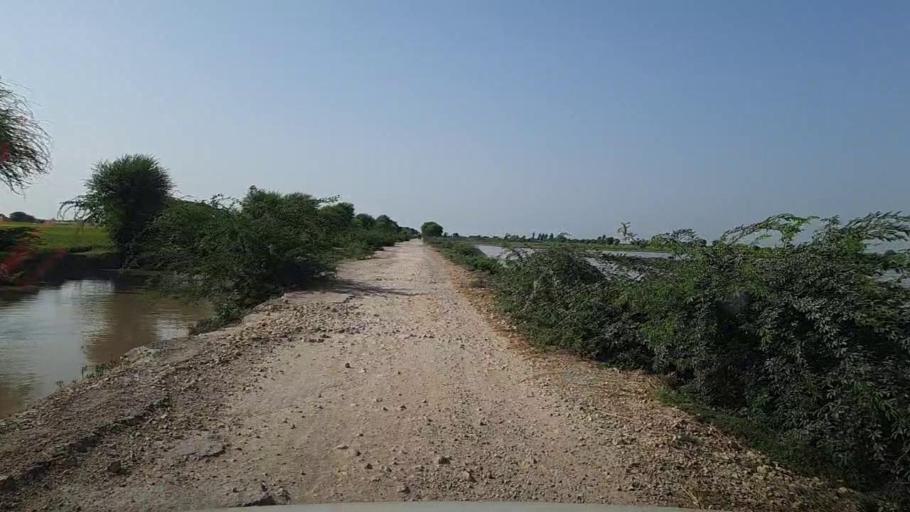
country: PK
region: Sindh
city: Kario
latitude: 24.7967
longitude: 68.5576
